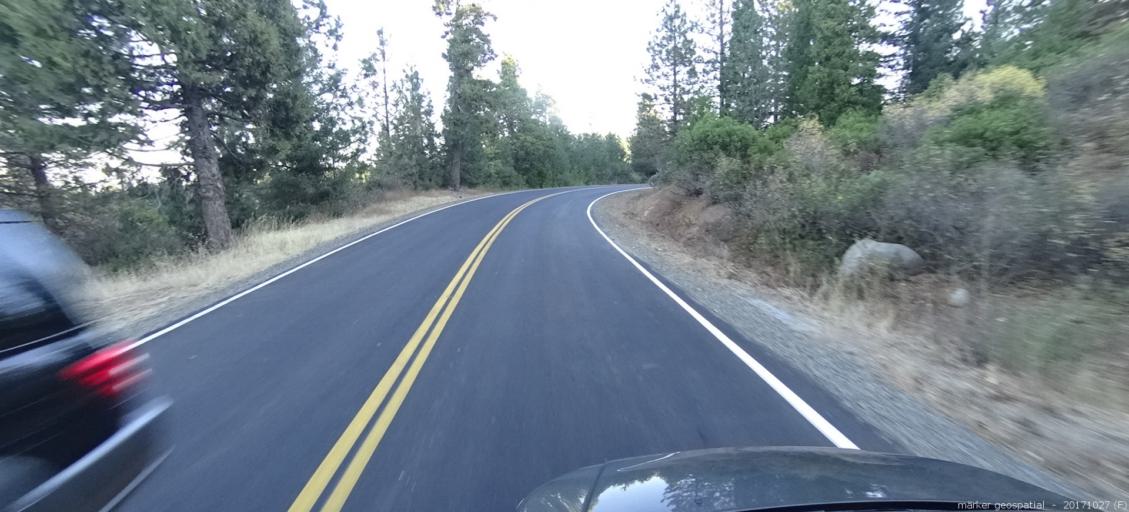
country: US
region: California
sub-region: Shasta County
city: Burney
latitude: 40.8683
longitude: -121.9025
